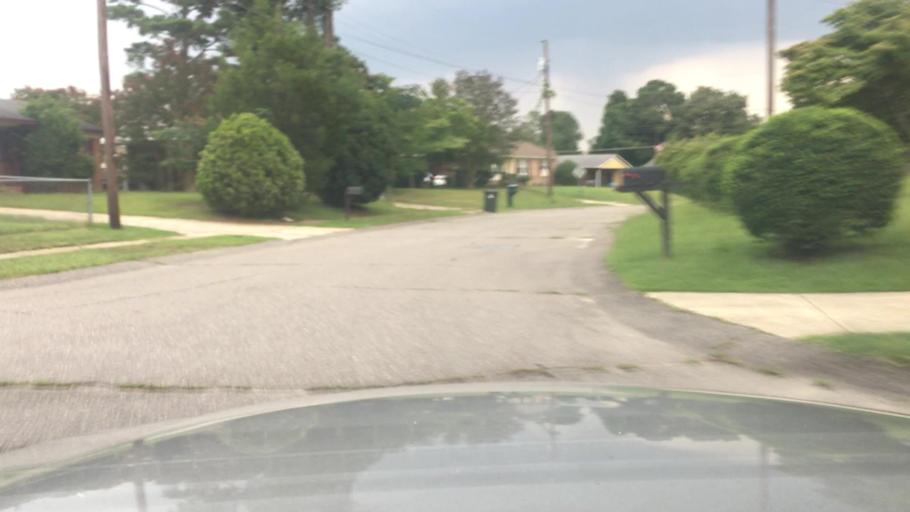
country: US
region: North Carolina
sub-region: Cumberland County
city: Fort Bragg
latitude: 35.0967
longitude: -78.9818
